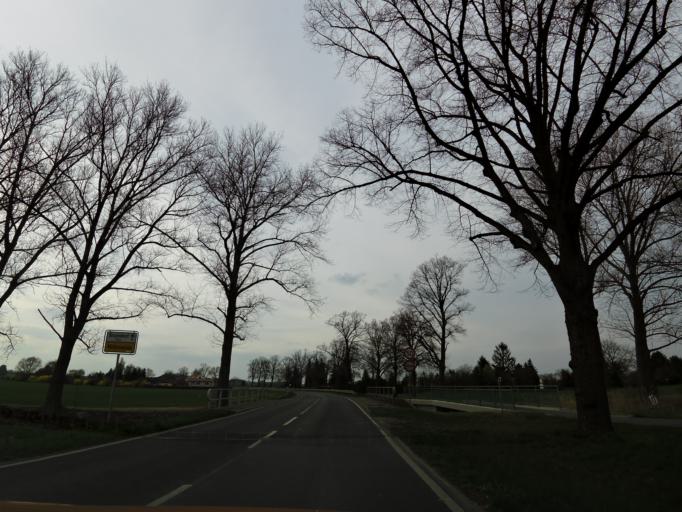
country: DE
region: Brandenburg
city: Mittenwalde
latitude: 52.2745
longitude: 13.5373
